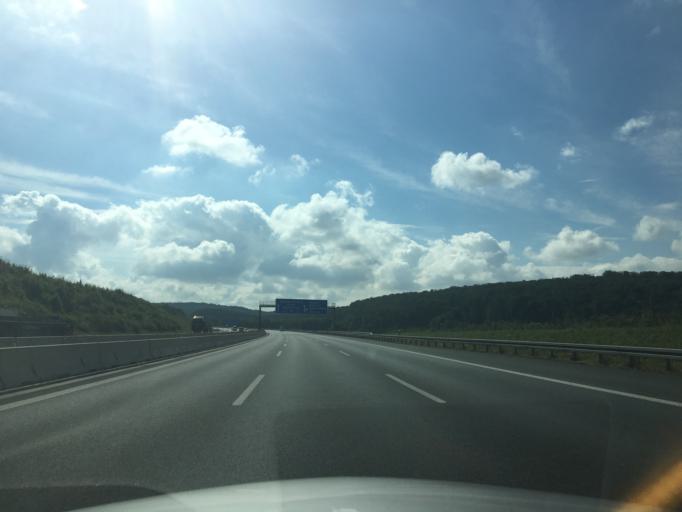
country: DE
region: Bavaria
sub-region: Regierungsbezirk Unterfranken
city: Waldbrunn
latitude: 49.7505
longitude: 9.7951
